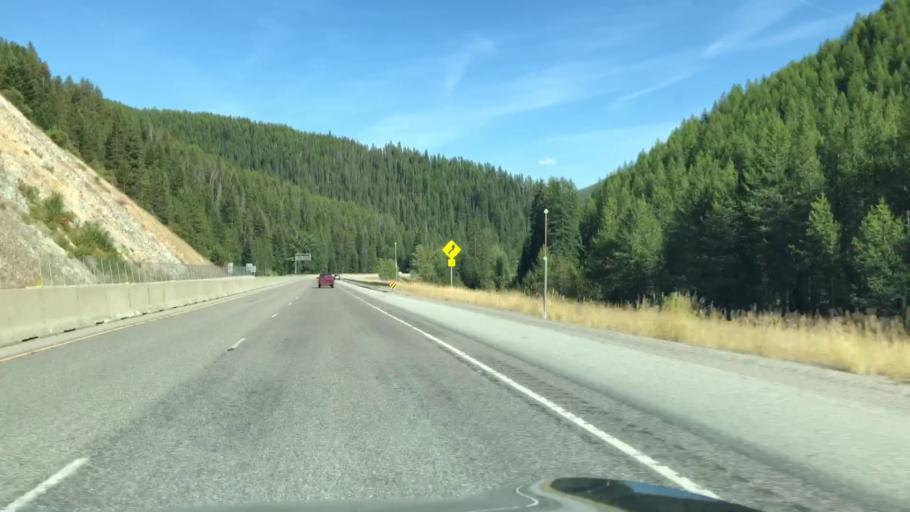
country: US
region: Montana
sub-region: Sanders County
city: Thompson Falls
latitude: 47.4187
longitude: -115.5976
